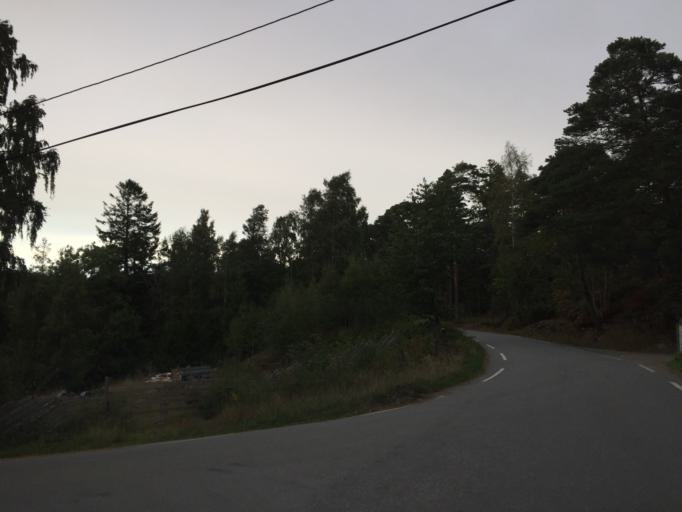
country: NO
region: Ostfold
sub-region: Hvaler
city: Skjaerhalden
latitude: 59.0587
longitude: 11.0077
